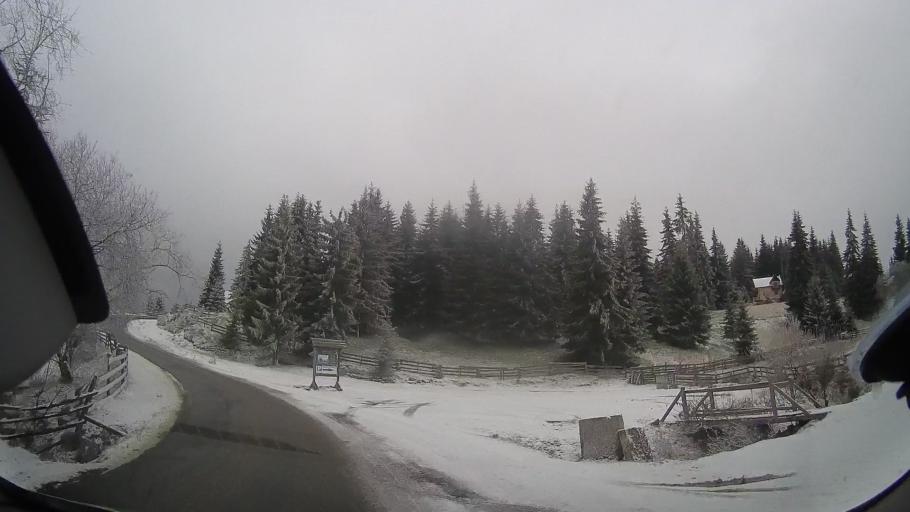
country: RO
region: Cluj
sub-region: Comuna Marisel
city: Marisel
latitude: 46.6614
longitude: 23.1033
